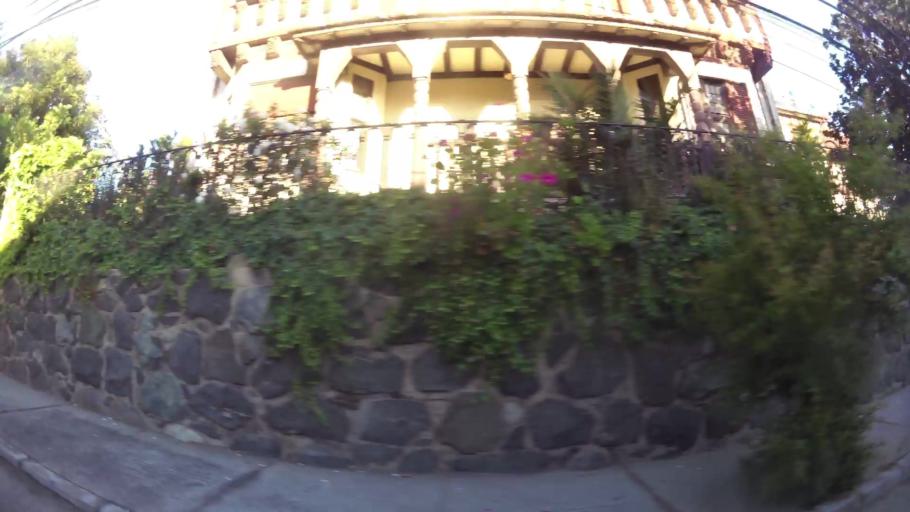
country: CL
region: Valparaiso
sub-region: Provincia de Valparaiso
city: Vina del Mar
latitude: -33.0219
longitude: -71.5650
